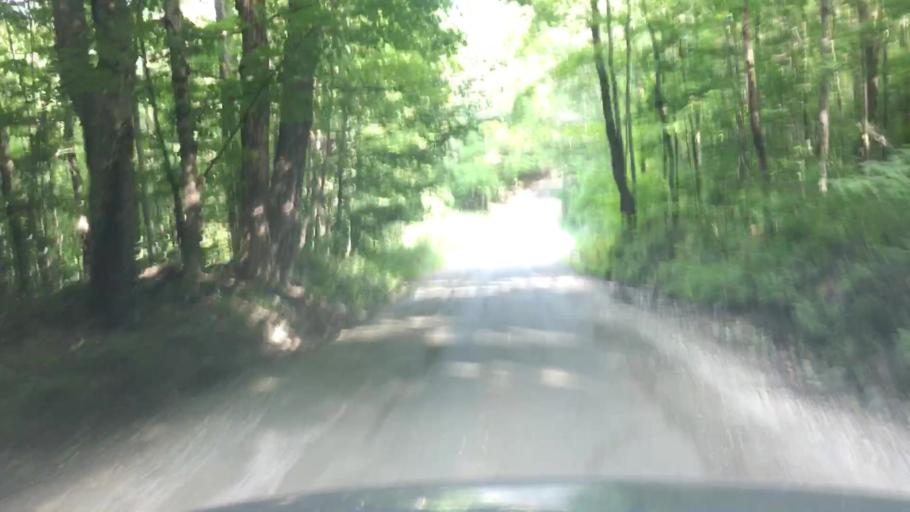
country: US
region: Vermont
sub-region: Windham County
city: Dover
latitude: 42.8220
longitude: -72.7676
